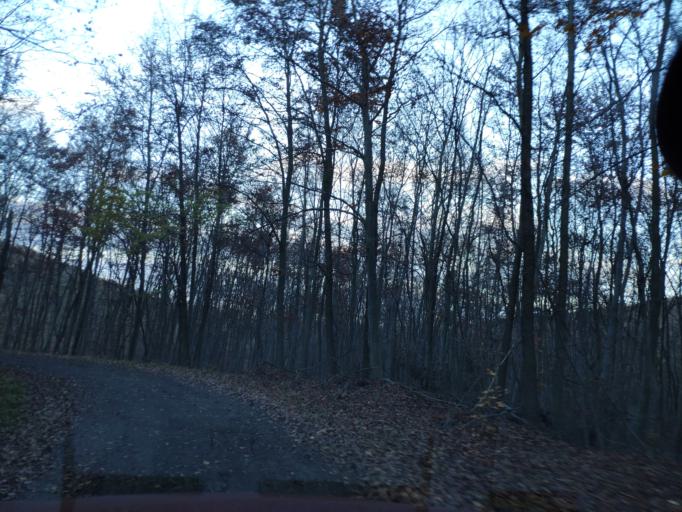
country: SK
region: Kosicky
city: Secovce
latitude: 48.6010
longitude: 21.5145
